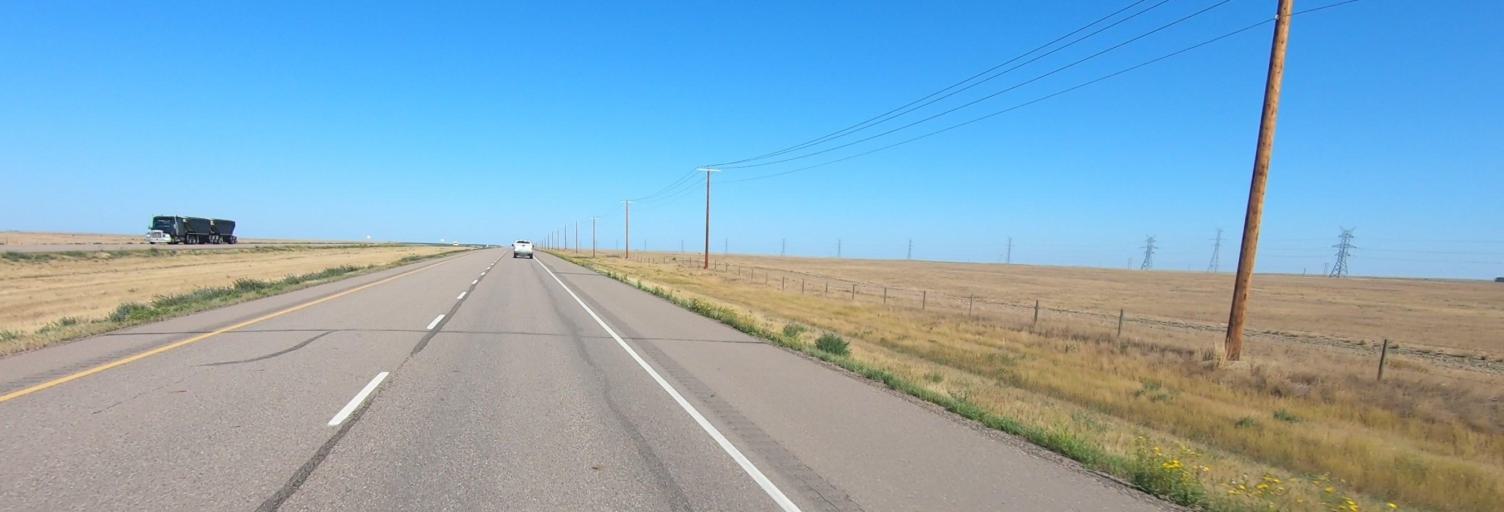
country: CA
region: Alberta
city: Bow Island
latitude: 50.2374
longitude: -111.2076
